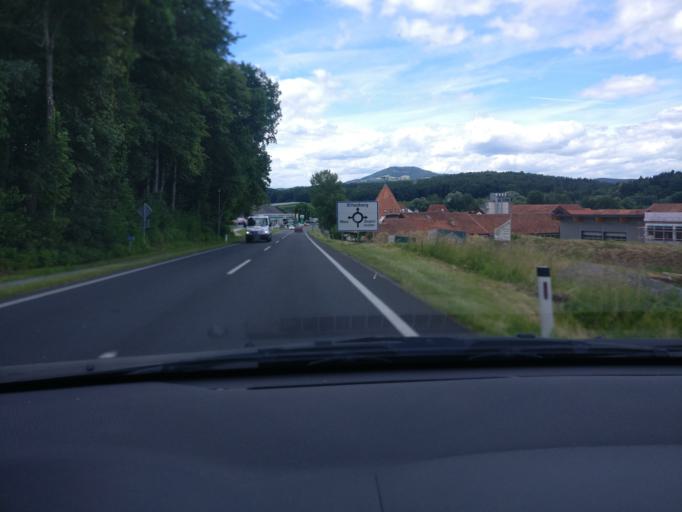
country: AT
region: Styria
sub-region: Politischer Bezirk Weiz
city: Oberrettenbach
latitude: 47.1473
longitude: 15.7706
